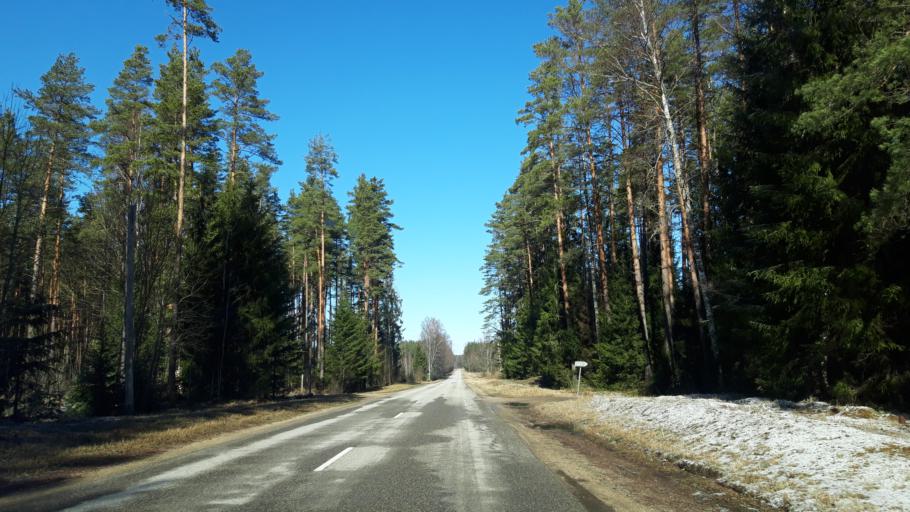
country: LV
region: Strenci
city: Strenci
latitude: 57.6022
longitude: 25.7156
